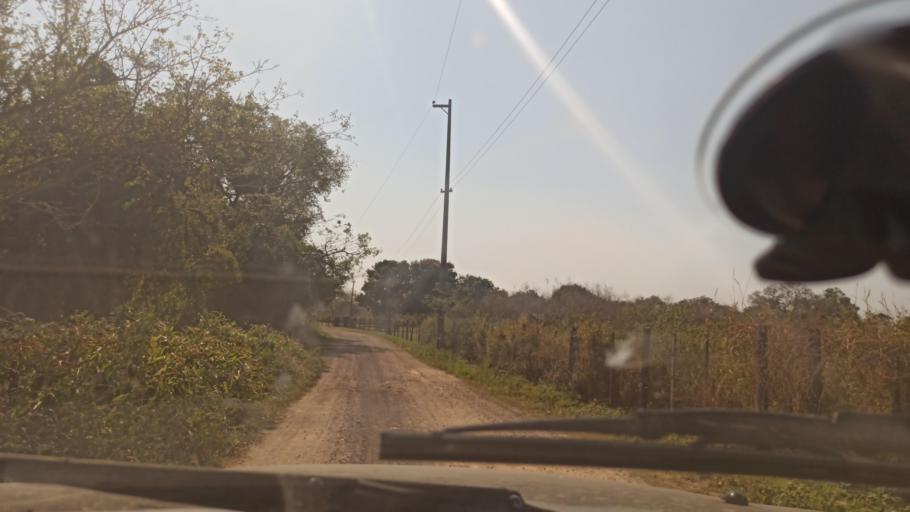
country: AR
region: Formosa
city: Clorinda
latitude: -25.3261
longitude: -57.6918
